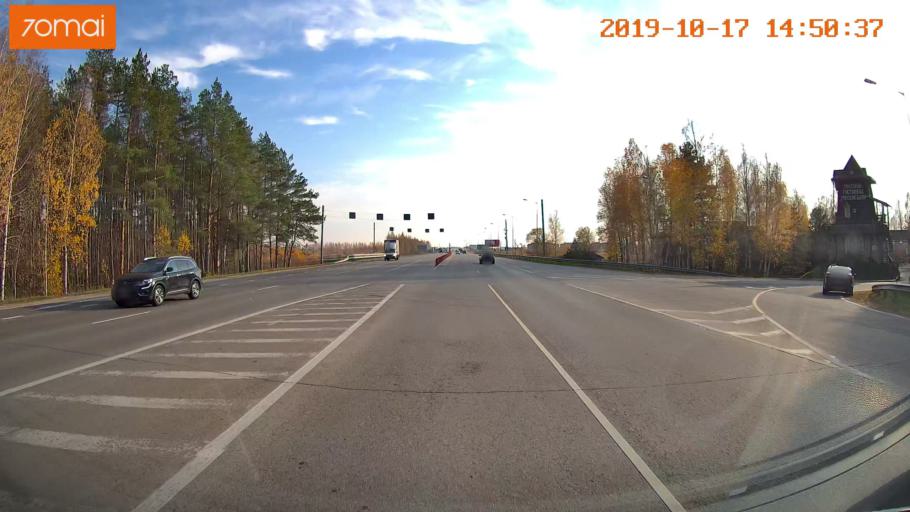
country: RU
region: Rjazan
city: Polyany
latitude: 54.7314
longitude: 39.8435
